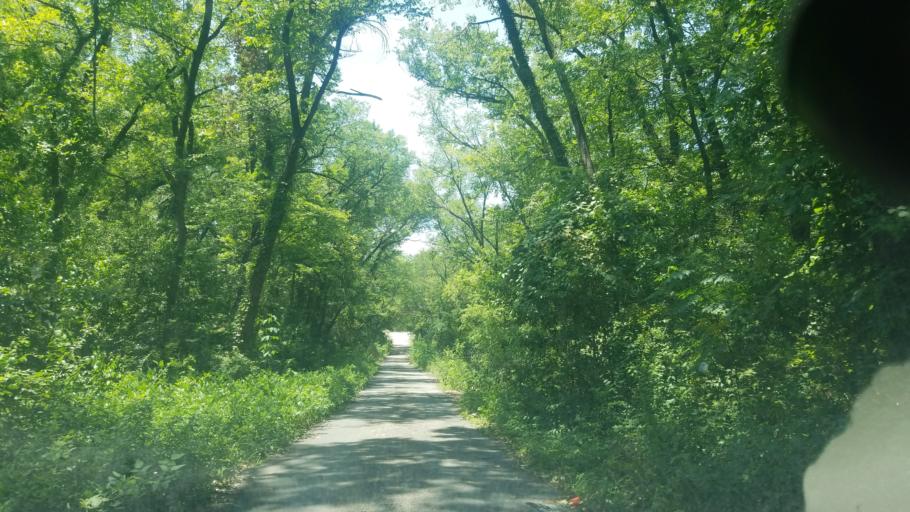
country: US
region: Texas
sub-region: Dallas County
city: Dallas
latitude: 32.7302
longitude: -96.7892
